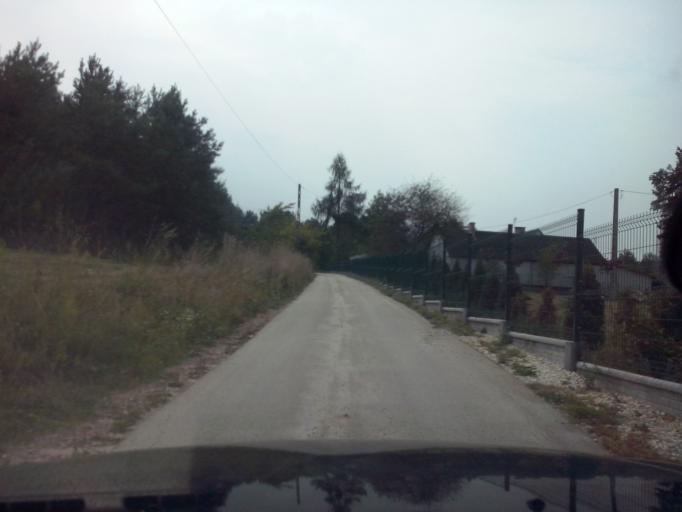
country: PL
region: Swietokrzyskie
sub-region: Powiat kielecki
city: Brzeziny
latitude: 50.7511
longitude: 20.5453
